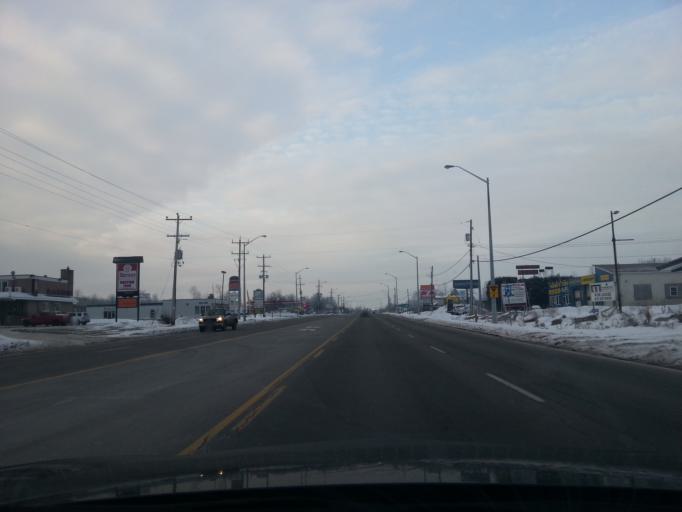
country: CA
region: Ontario
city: Carleton Place
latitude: 45.1310
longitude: -76.1220
